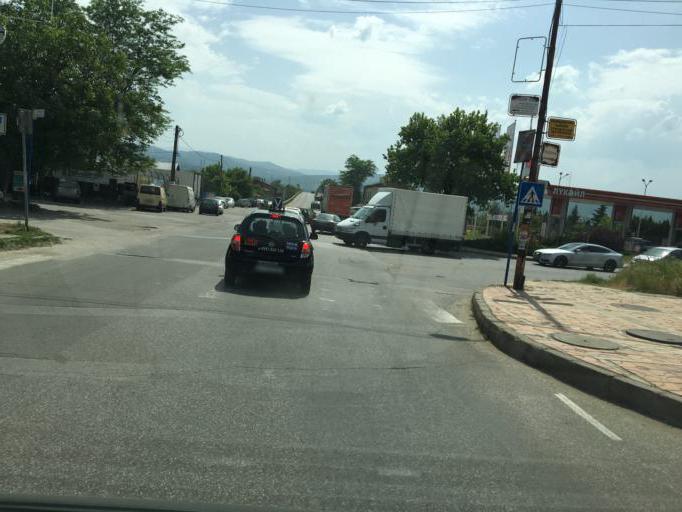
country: BG
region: Blagoevgrad
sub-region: Obshtina Blagoevgrad
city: Blagoevgrad
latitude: 42.0064
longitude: 23.0843
